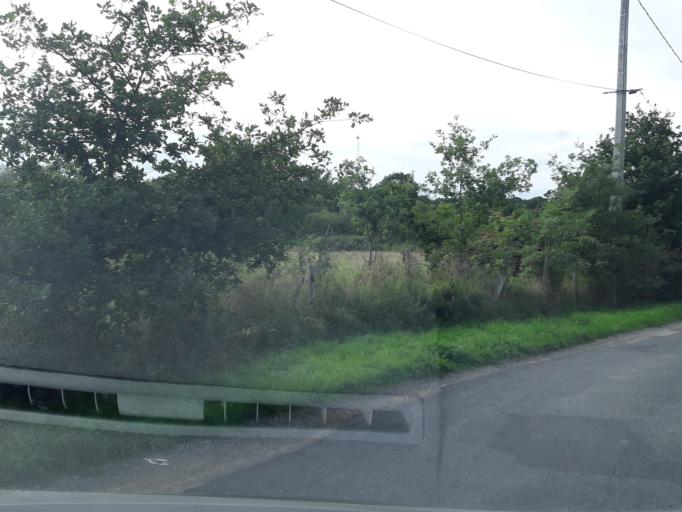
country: FR
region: Centre
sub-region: Departement du Loiret
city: Chilleurs-aux-Bois
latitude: 48.0492
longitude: 2.1639
